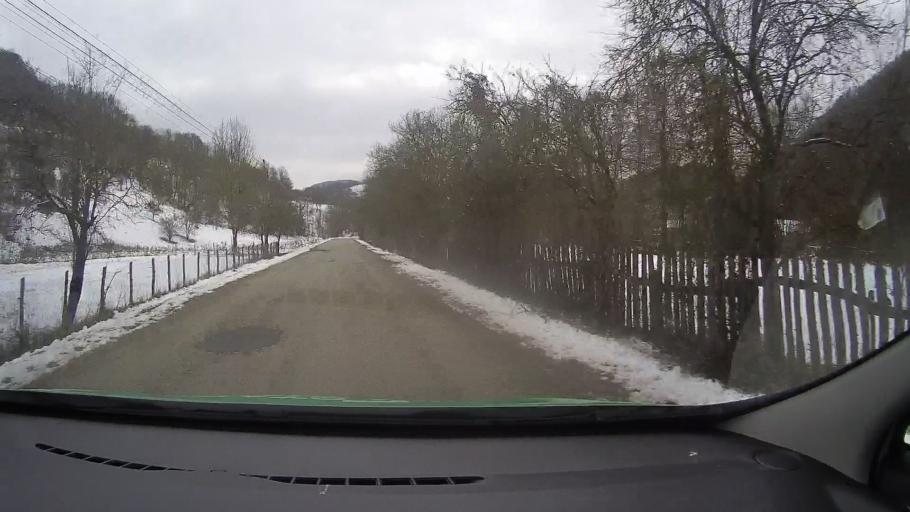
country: RO
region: Hunedoara
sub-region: Comuna Balsa
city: Balsa
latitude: 46.0501
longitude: 23.0708
